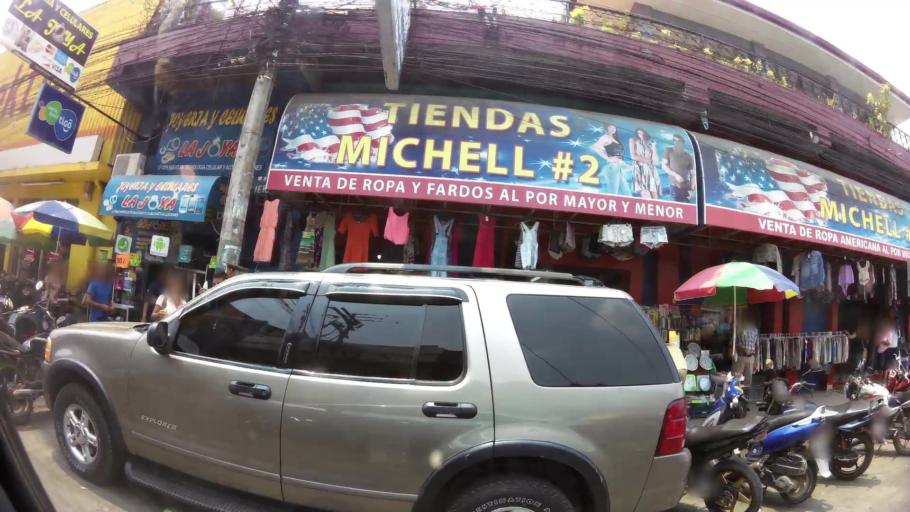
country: HN
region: Yoro
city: El Progreso
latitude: 15.4015
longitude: -87.8087
